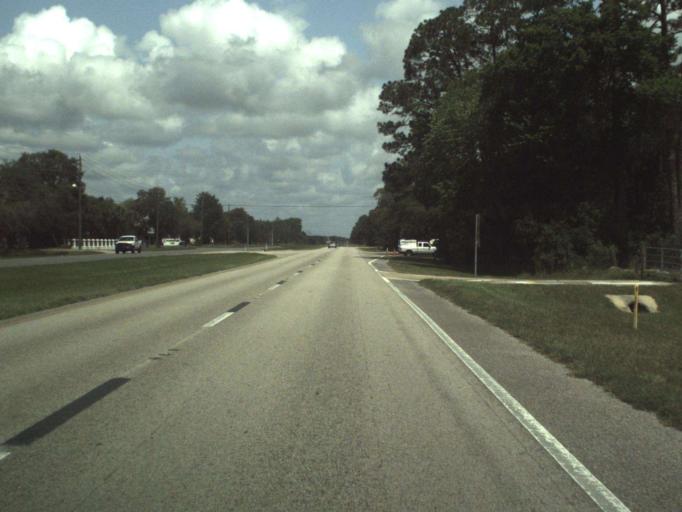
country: US
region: Florida
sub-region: Volusia County
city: Ormond-by-the-Sea
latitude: 29.3460
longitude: -81.1447
